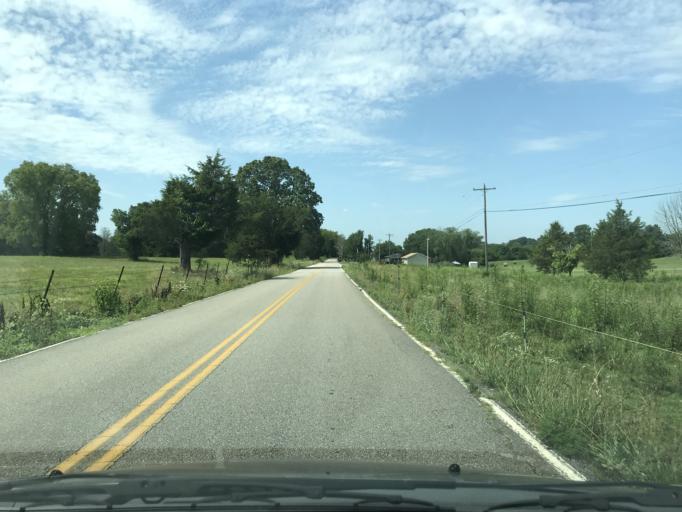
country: US
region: Tennessee
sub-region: Hamilton County
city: Lakesite
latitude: 35.1866
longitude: -85.0373
